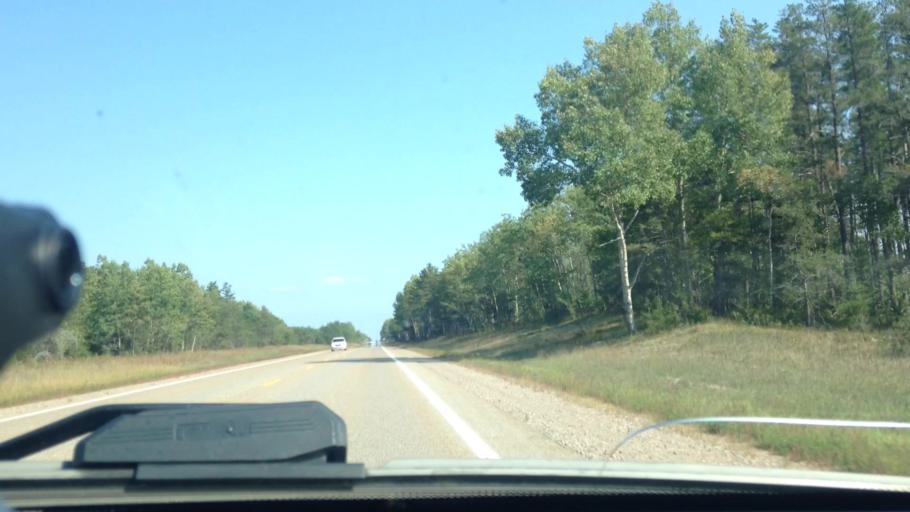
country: US
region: Michigan
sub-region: Mackinac County
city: Saint Ignace
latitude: 46.3583
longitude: -84.8764
